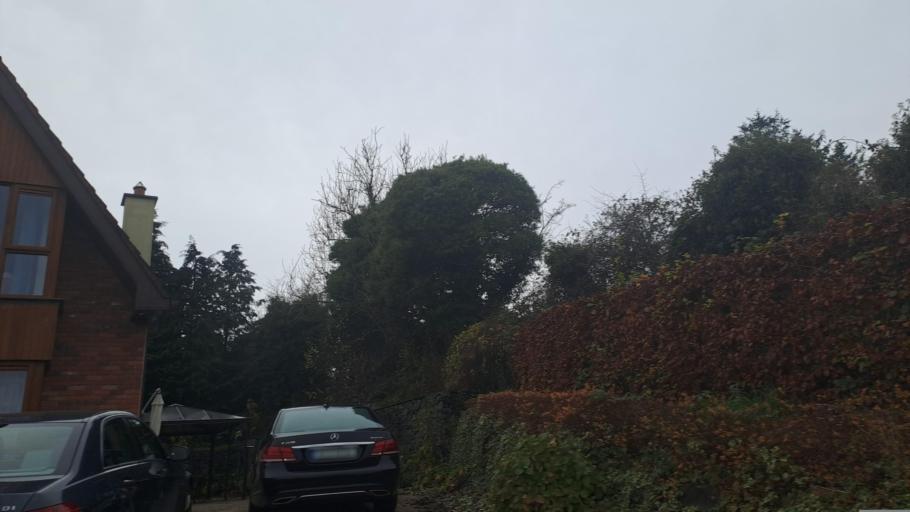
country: IE
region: Ulster
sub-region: An Cabhan
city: Virginia
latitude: 53.8392
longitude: -7.0889
